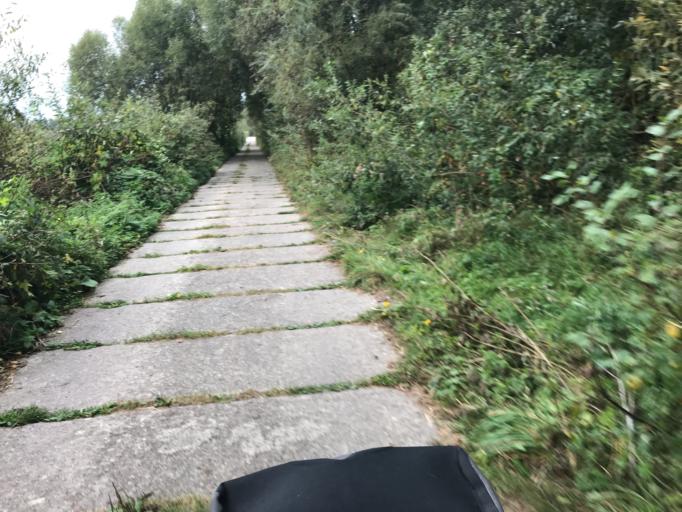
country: PL
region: Podlasie
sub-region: Powiat bialostocki
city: Choroszcz
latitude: 53.1380
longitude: 22.8726
